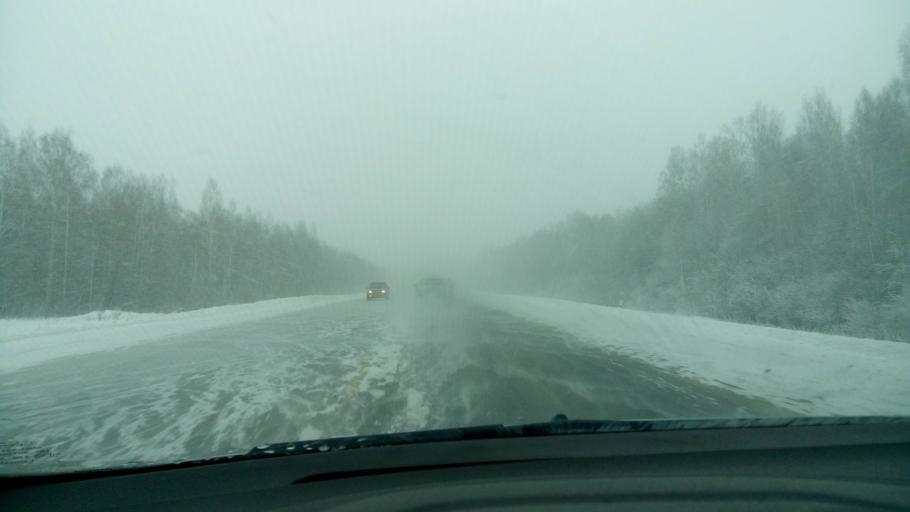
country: RU
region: Sverdlovsk
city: Bogdanovich
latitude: 56.7748
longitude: 61.9654
